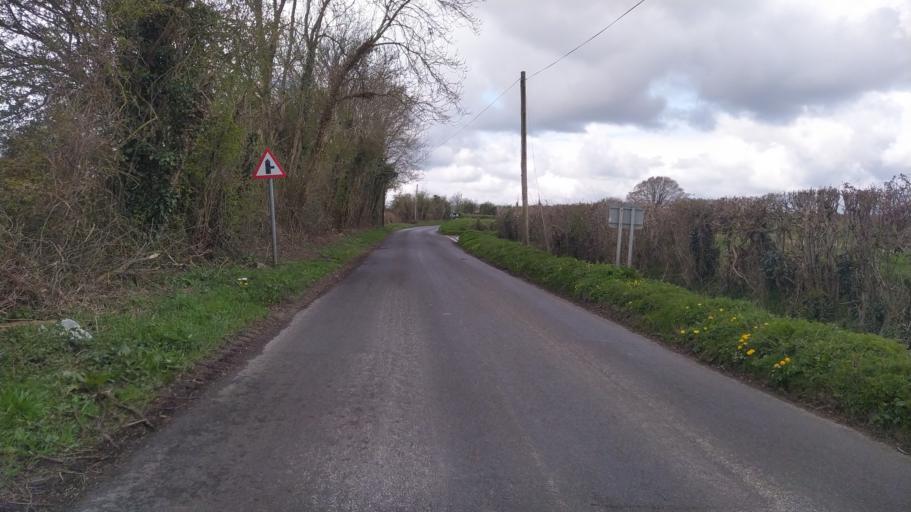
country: GB
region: England
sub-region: Wiltshire
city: Bratton
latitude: 51.2904
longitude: -2.1582
